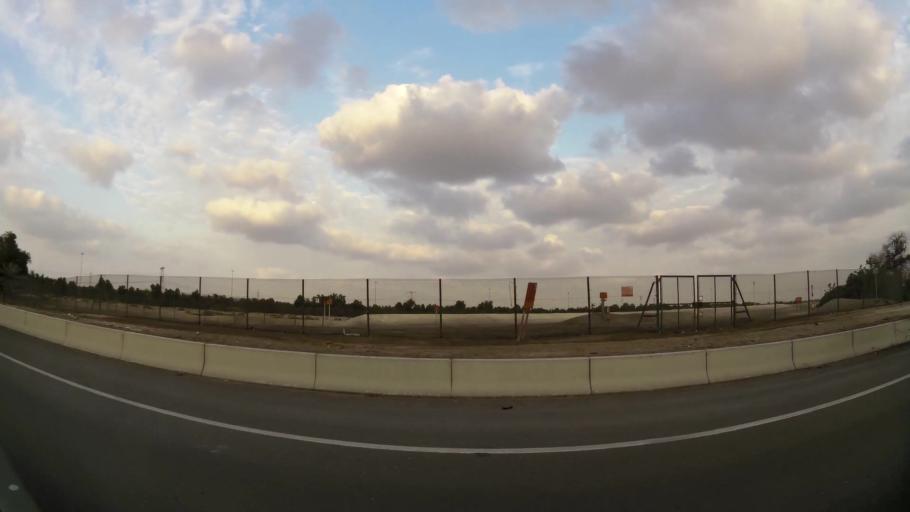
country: AE
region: Abu Dhabi
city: Abu Dhabi
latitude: 24.4022
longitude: 54.5235
